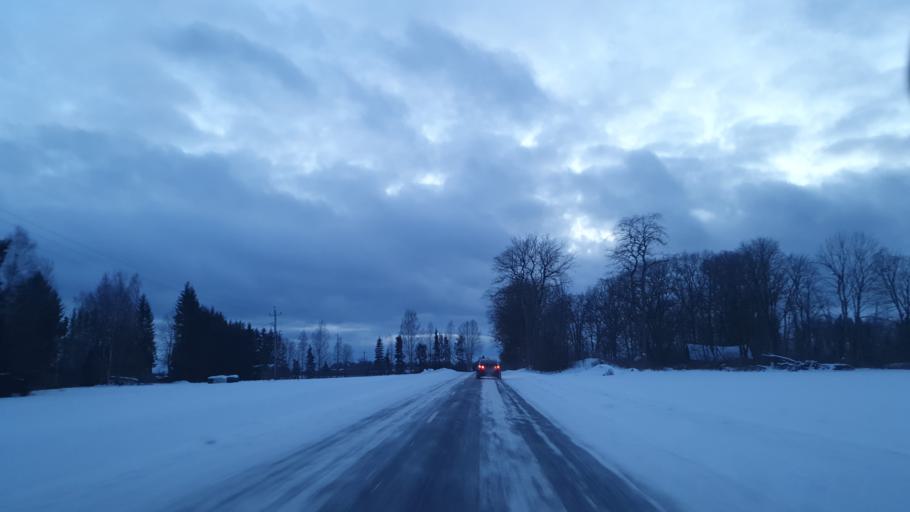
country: EE
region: Jogevamaa
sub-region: Jogeva linn
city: Jogeva
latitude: 58.5844
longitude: 26.3175
